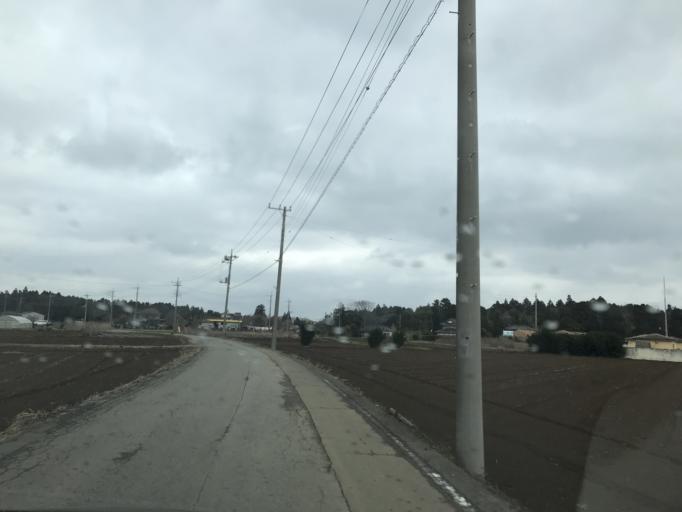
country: JP
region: Chiba
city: Sawara
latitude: 35.8527
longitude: 140.5494
